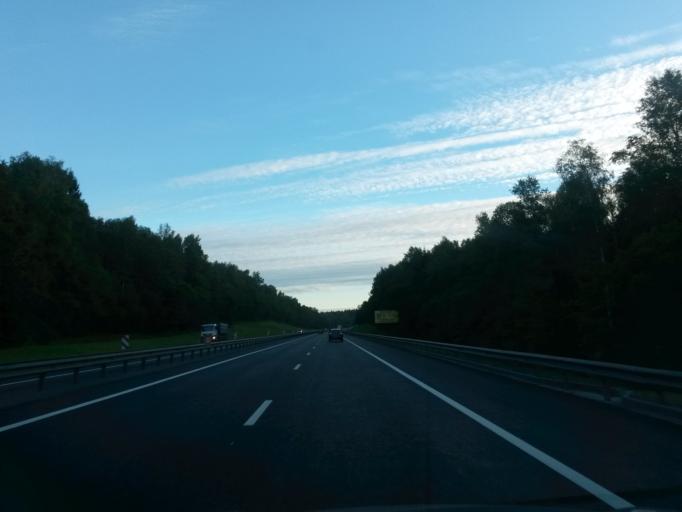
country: RU
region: Moskovskaya
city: Krasnozavodsk
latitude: 56.4478
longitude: 38.3466
